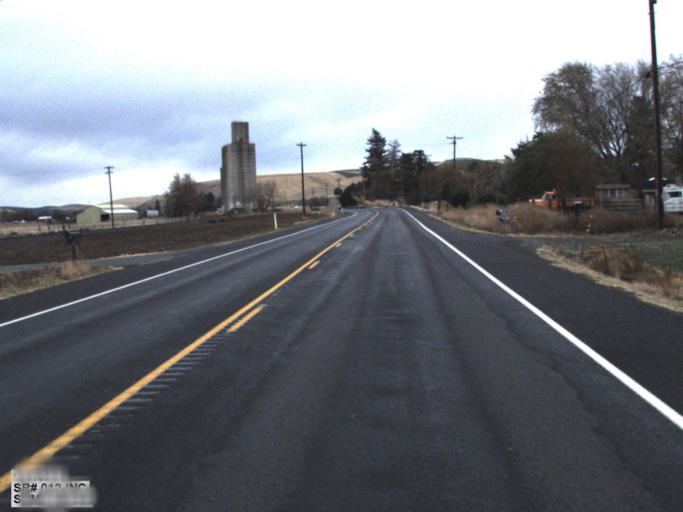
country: US
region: Washington
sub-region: Columbia County
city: Dayton
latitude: 46.2893
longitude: -118.0327
